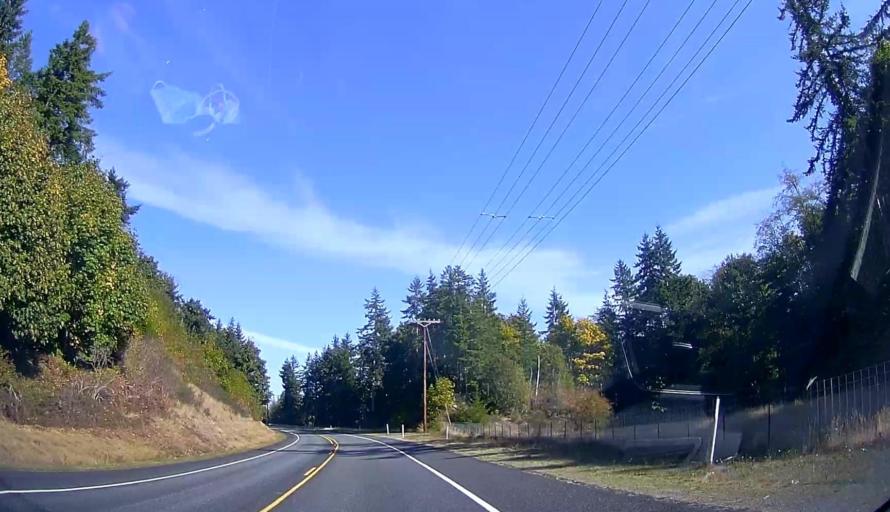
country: US
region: Washington
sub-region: Island County
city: Camano
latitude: 48.1908
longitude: -122.4943
